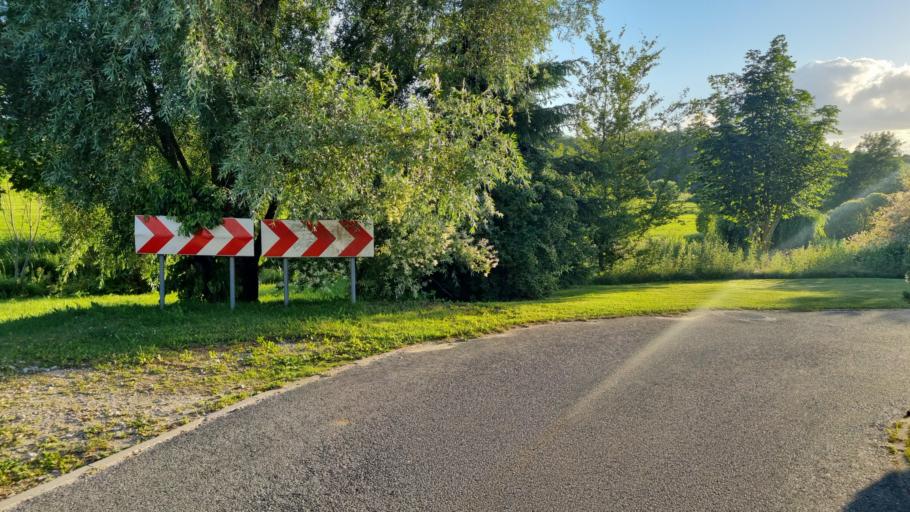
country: LV
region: Kekava
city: Balozi
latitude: 56.8902
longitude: 24.1650
